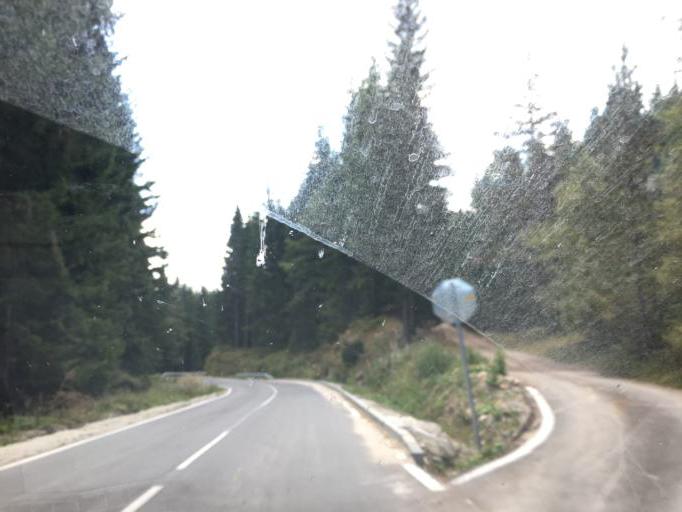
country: BG
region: Pazardzhik
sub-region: Obshtina Batak
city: Batak
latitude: 41.9037
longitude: 24.3015
